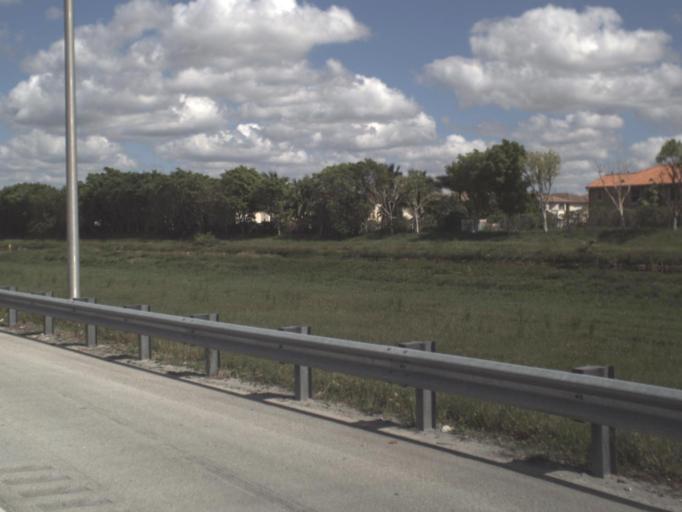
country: US
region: Florida
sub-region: Miami-Dade County
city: Doral
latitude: 25.8336
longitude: -80.3867
